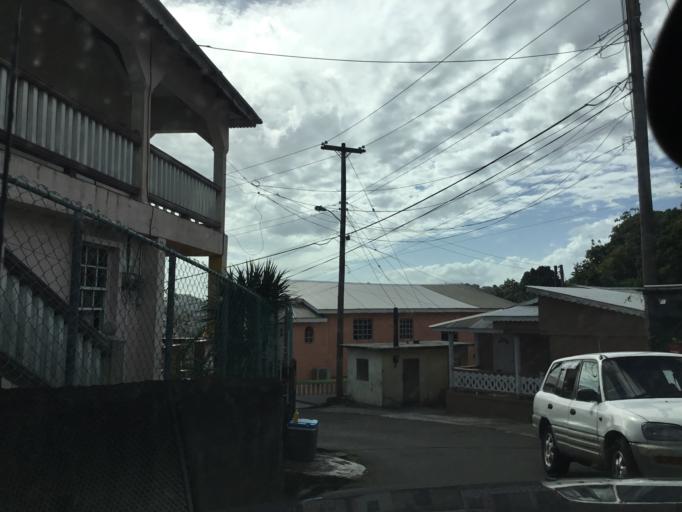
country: VC
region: Saint George
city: Kingstown
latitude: 13.1665
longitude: -61.2196
